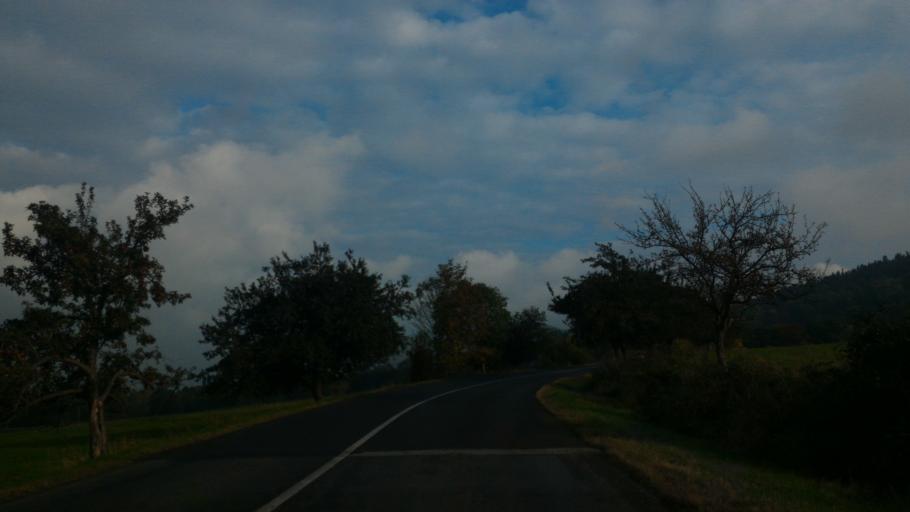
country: CZ
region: Ustecky
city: Dolni Podluzi
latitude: 50.8777
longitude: 14.5605
